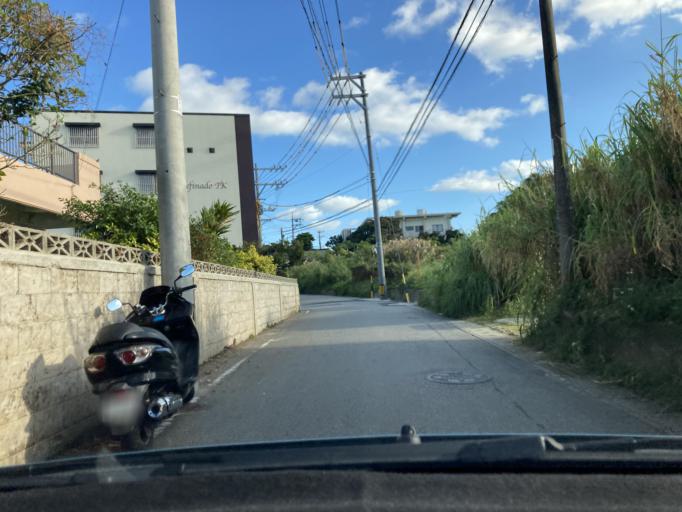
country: JP
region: Okinawa
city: Gushikawa
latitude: 26.3631
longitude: 127.8540
